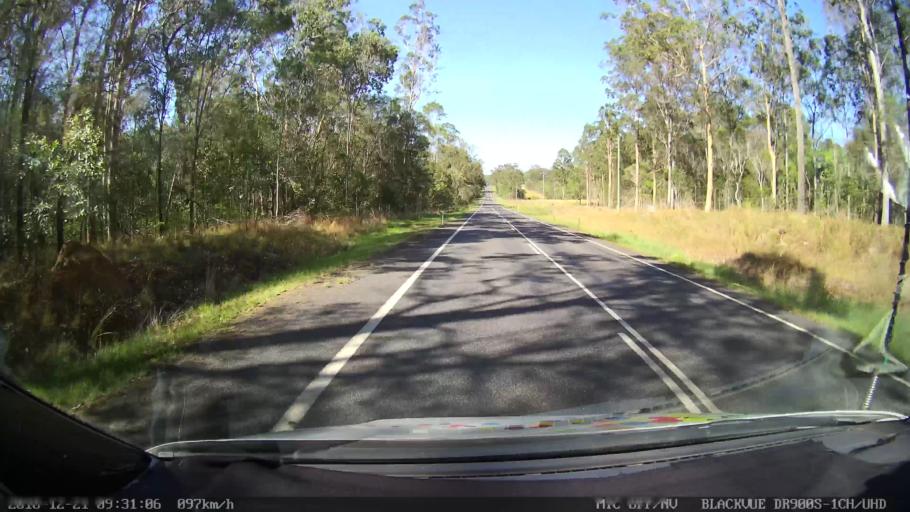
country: AU
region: New South Wales
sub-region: Clarence Valley
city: Maclean
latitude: -29.4561
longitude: 152.9926
